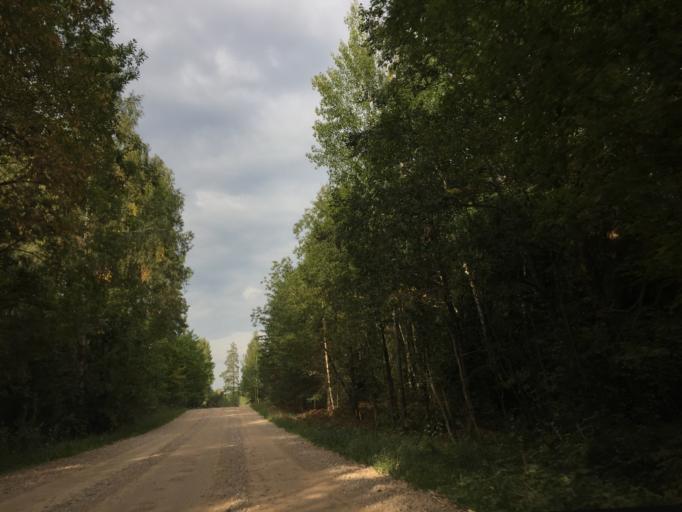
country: LV
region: Ikskile
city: Ikskile
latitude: 56.8088
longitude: 24.4453
